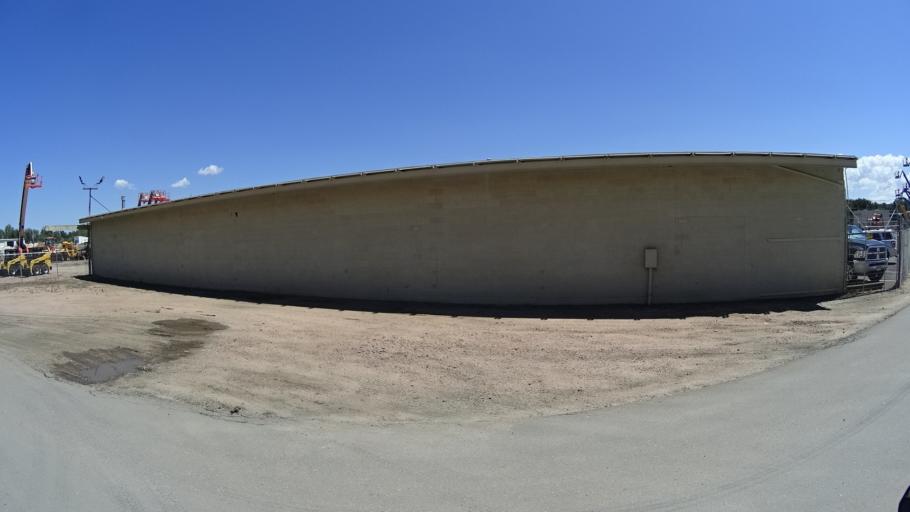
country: US
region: Colorado
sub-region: El Paso County
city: Colorado Springs
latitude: 38.8677
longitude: -104.8321
